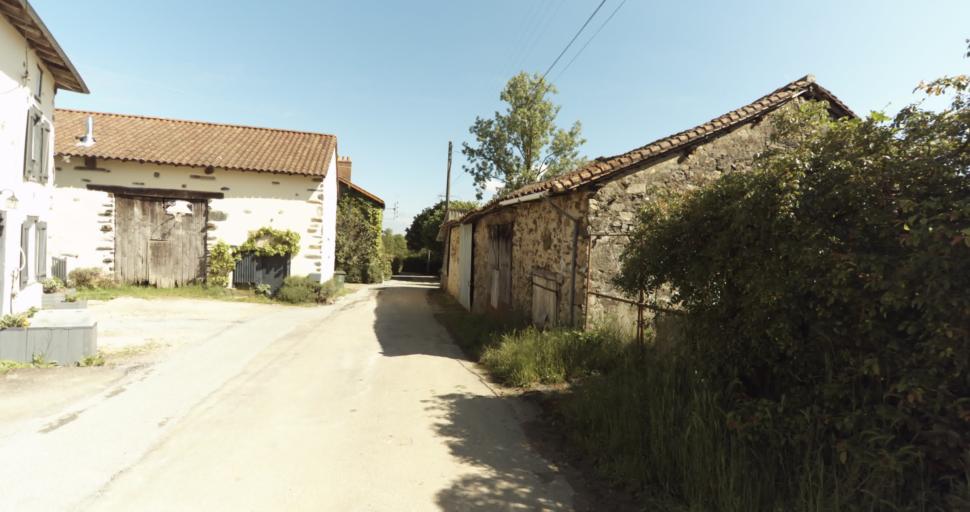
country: FR
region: Limousin
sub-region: Departement de la Haute-Vienne
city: Le Vigen
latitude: 45.7350
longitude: 1.2845
